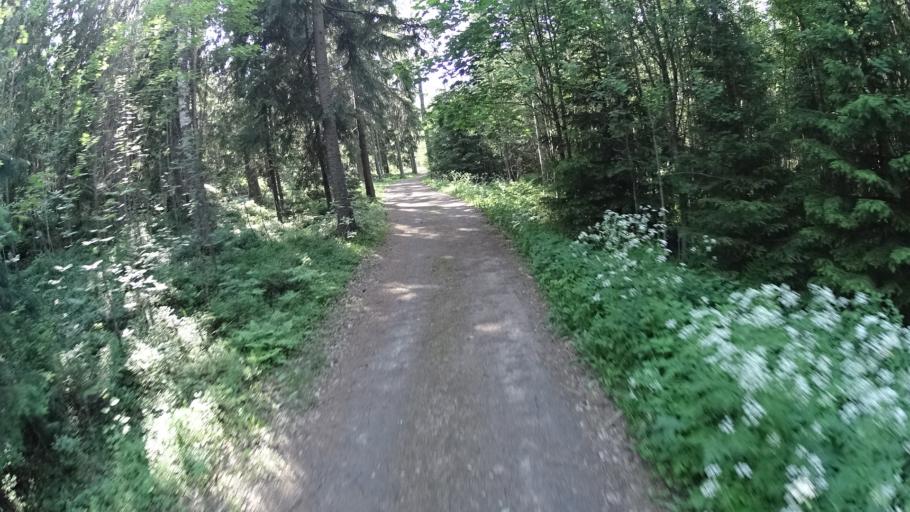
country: FI
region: Uusimaa
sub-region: Helsinki
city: Vantaa
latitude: 60.2363
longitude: 25.1756
